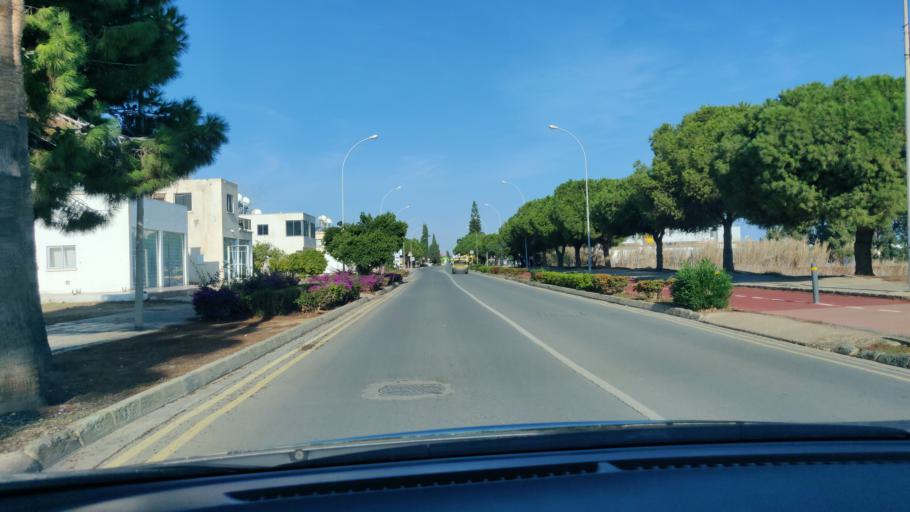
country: CY
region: Ammochostos
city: Protaras
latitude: 35.0121
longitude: 34.0518
